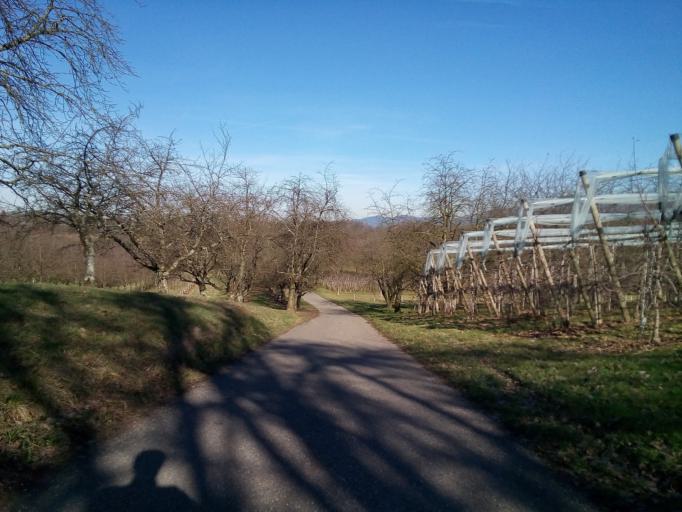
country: DE
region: Baden-Wuerttemberg
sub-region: Freiburg Region
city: Achern
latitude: 48.6061
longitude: 8.0576
